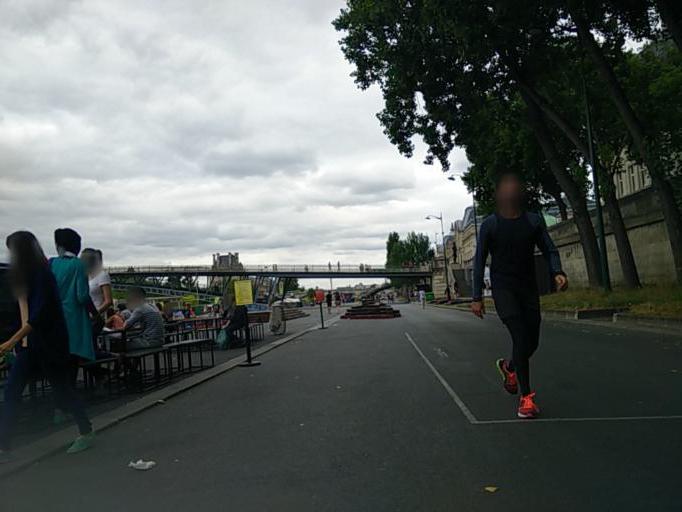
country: FR
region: Ile-de-France
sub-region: Paris
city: Paris
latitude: 48.8616
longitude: 2.3231
